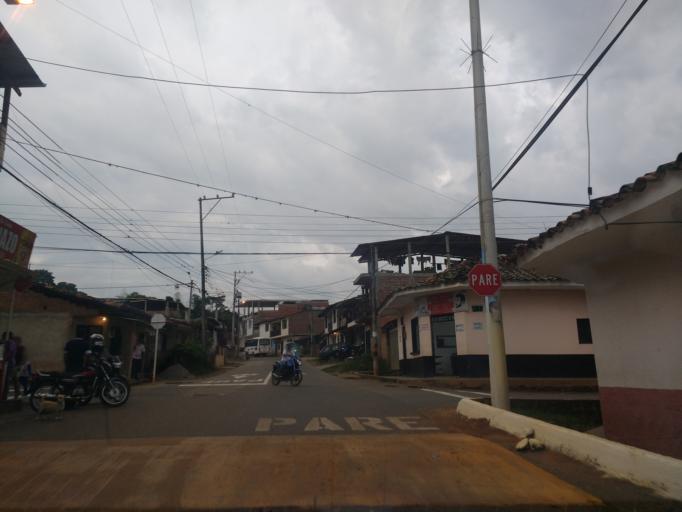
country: CO
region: Cauca
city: Santander de Quilichao
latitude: 3.0020
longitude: -76.4762
